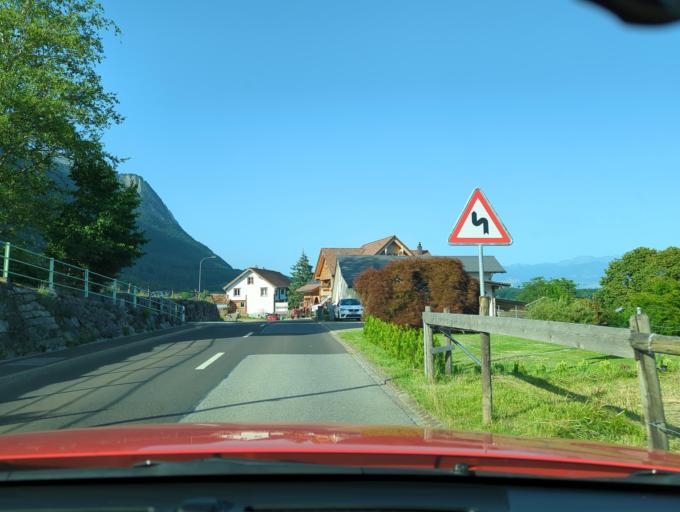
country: CH
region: Saint Gallen
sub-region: Wahlkreis Werdenberg
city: Haag (Rheintal)
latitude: 47.2385
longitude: 9.4647
